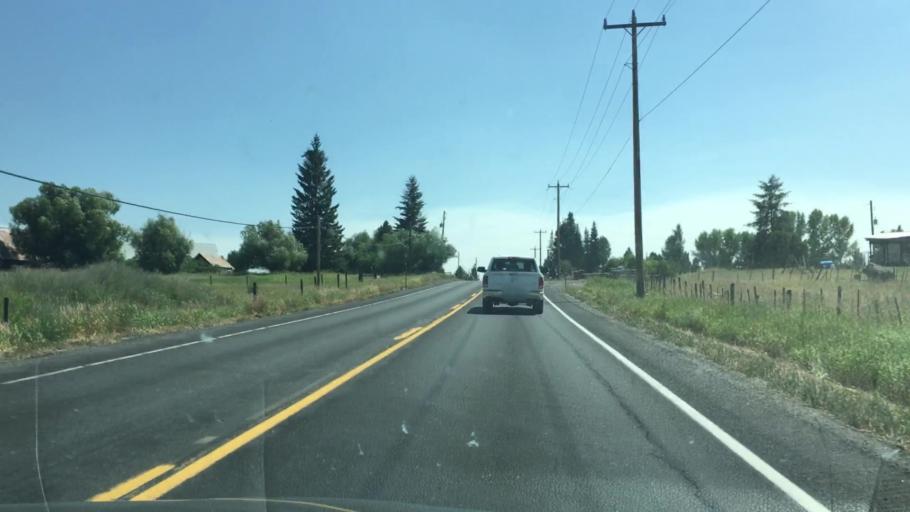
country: US
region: Idaho
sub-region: Valley County
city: McCall
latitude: 44.8732
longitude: -116.0908
